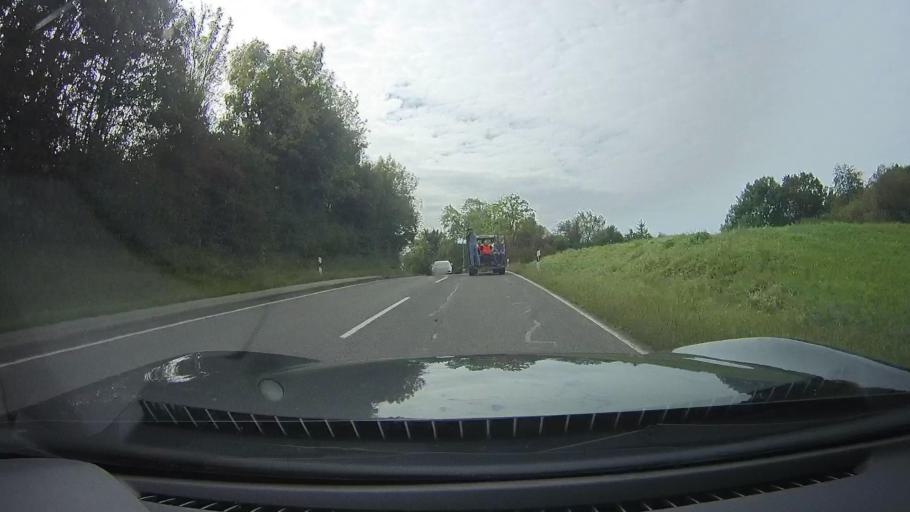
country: DE
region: Baden-Wuerttemberg
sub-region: Regierungsbezirk Stuttgart
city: Oberstenfeld
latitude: 49.0365
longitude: 9.3353
